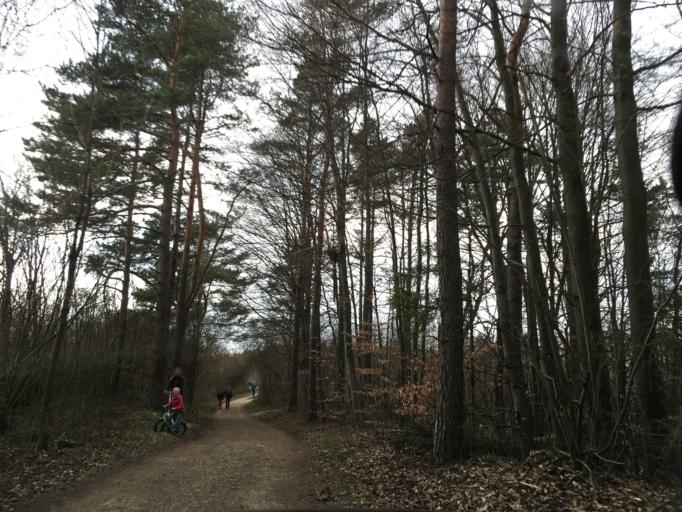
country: DE
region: Bavaria
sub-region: Upper Franconia
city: Pottenstein
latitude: 49.7618
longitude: 11.4300
